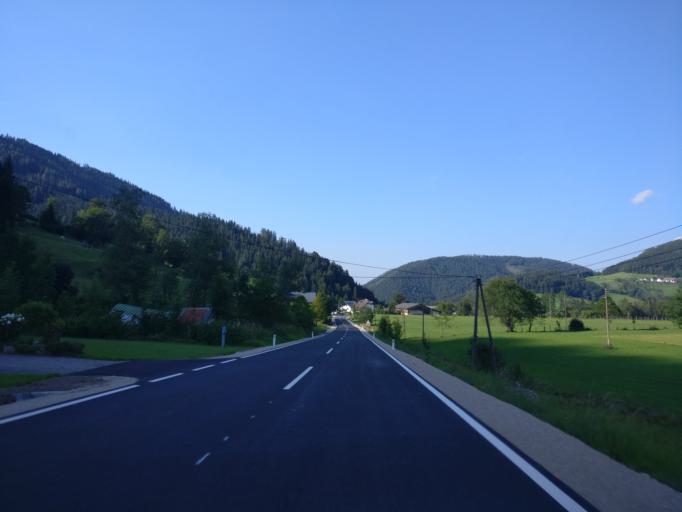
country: AT
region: Lower Austria
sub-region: Politischer Bezirk Scheibbs
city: Gostling an der Ybbs
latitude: 47.7503
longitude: 14.8992
